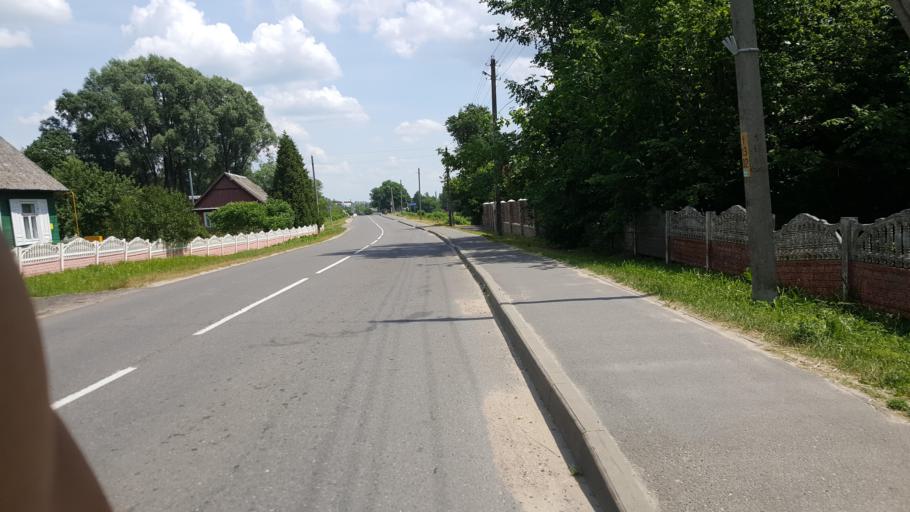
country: BY
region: Brest
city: Kamyanyets
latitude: 52.4018
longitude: 23.7994
